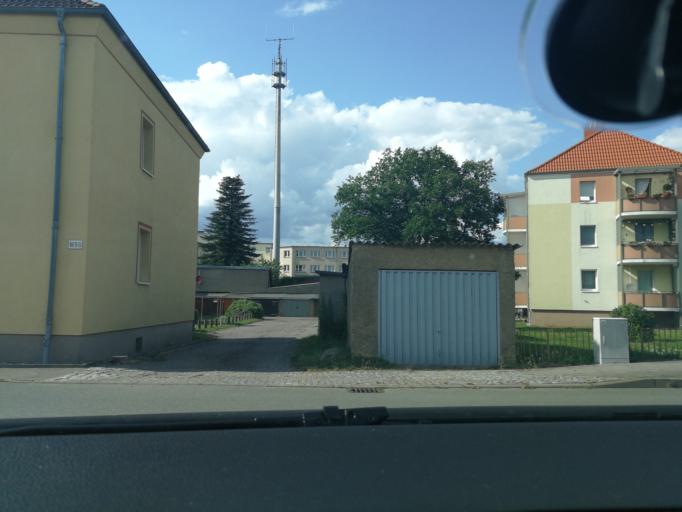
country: DE
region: Brandenburg
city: Pritzwalk
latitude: 53.1466
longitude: 12.1856
